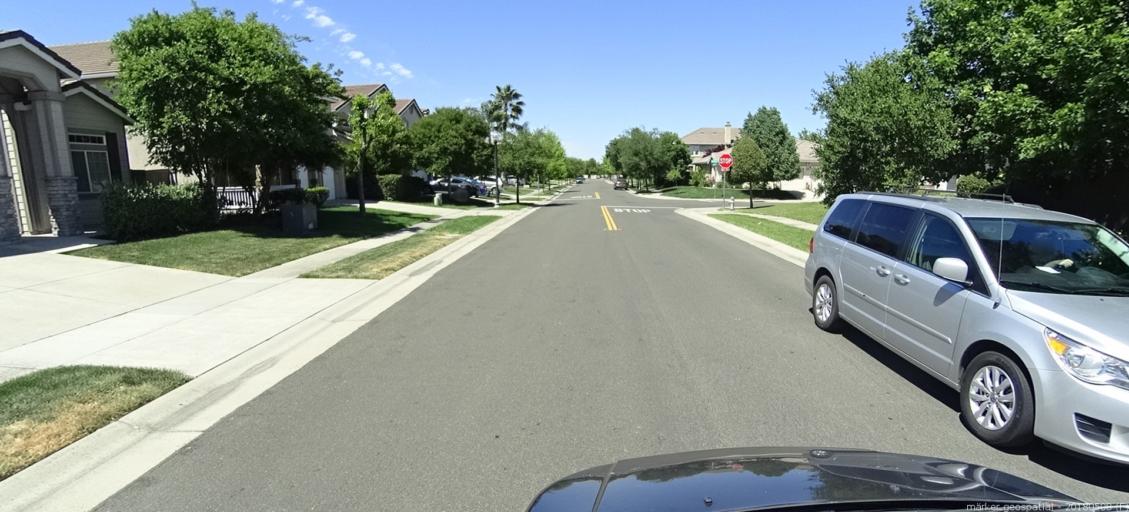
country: US
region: California
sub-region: Sacramento County
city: Elverta
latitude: 38.6778
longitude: -121.5254
